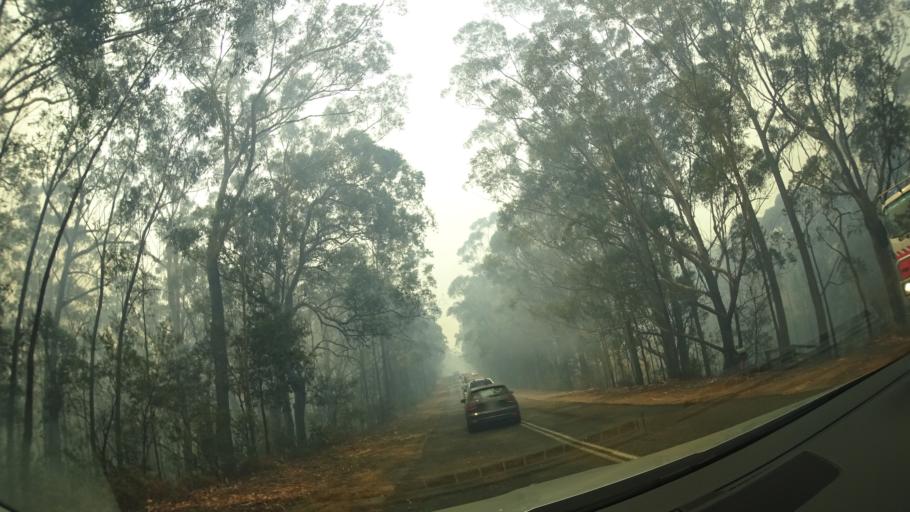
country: AU
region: New South Wales
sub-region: Shoalhaven Shire
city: Milton
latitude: -35.2115
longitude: 150.4598
